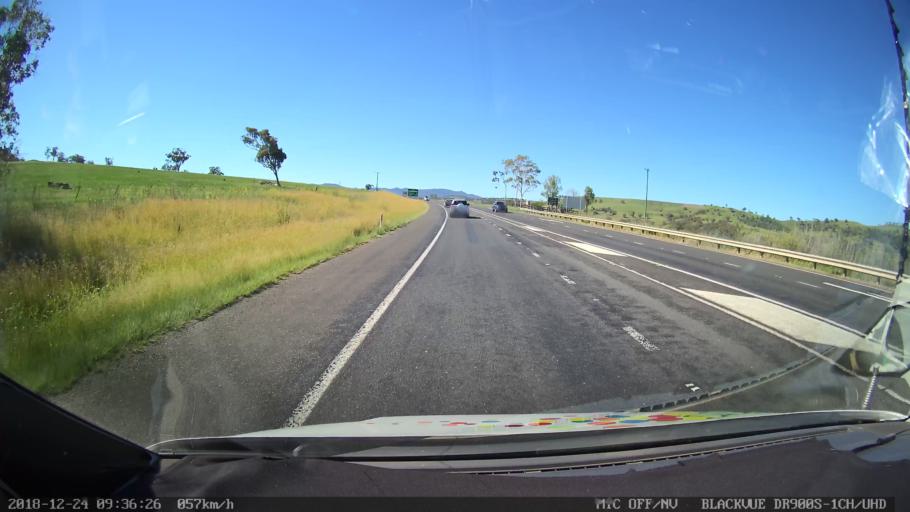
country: AU
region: New South Wales
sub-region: Liverpool Plains
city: Quirindi
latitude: -31.6377
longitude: 150.7222
